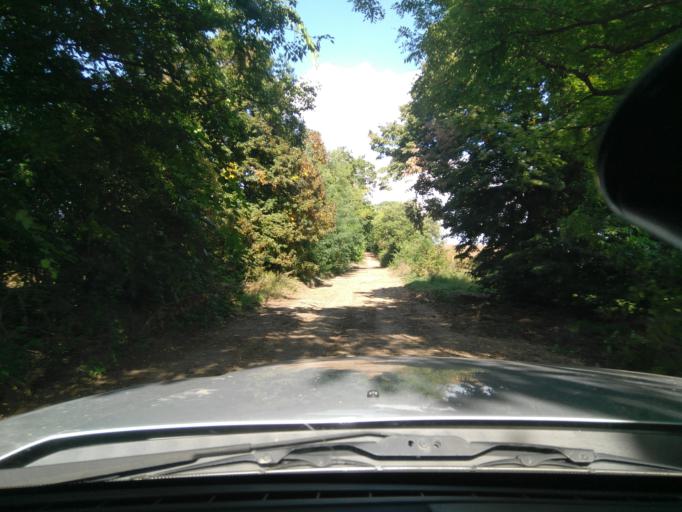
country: HU
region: Fejer
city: Bicske
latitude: 47.4401
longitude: 18.6468
